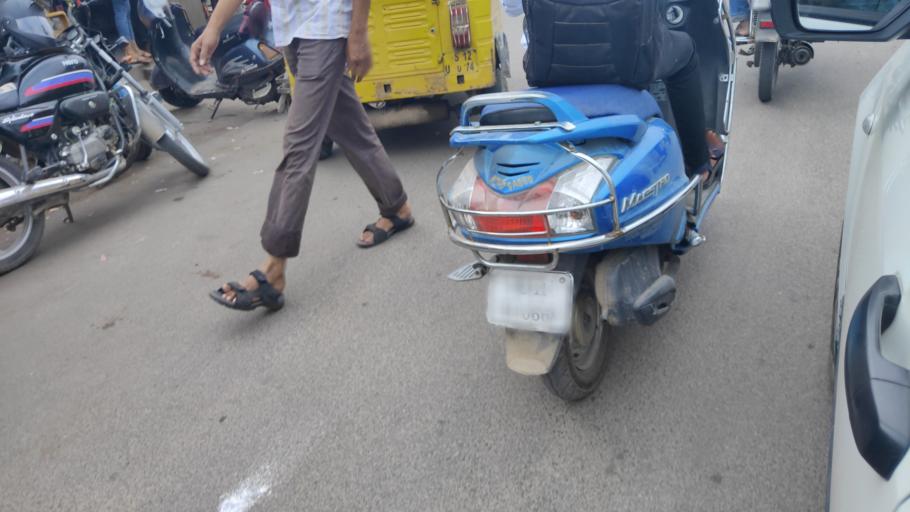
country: IN
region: Telangana
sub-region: Hyderabad
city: Hyderabad
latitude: 17.3678
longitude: 78.4859
